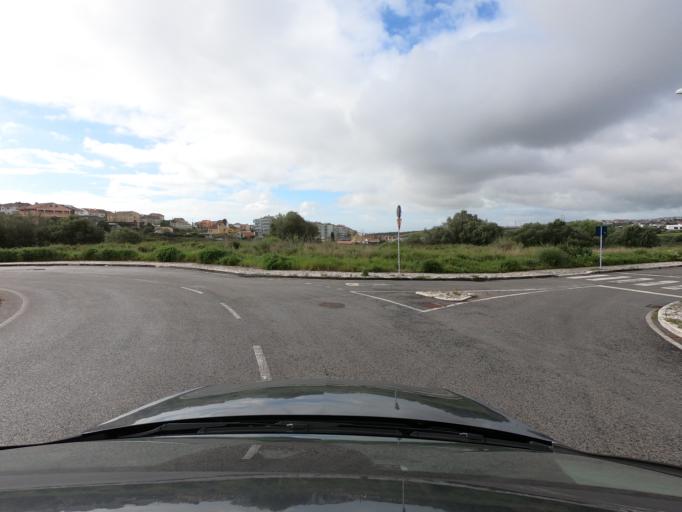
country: PT
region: Lisbon
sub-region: Oeiras
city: Porto Salvo
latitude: 38.7284
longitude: -9.3138
